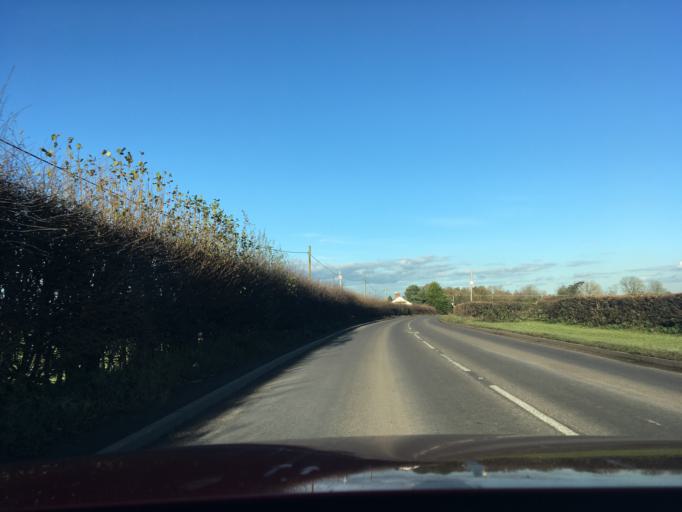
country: GB
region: England
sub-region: Staffordshire
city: Uttoxeter
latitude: 52.8641
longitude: -1.7646
